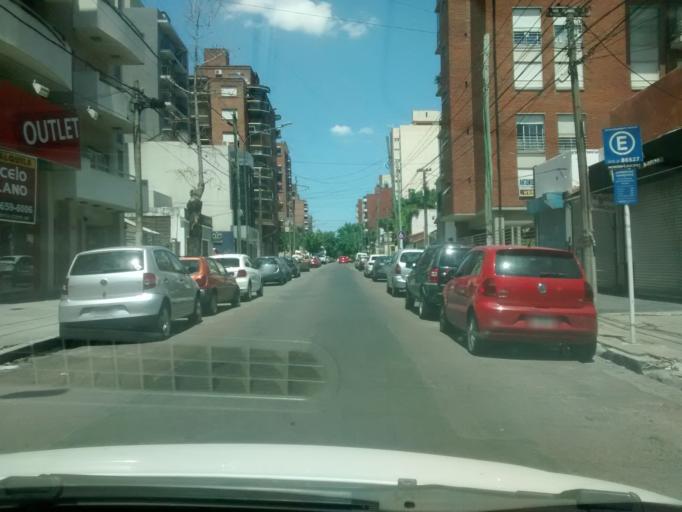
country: AR
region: Buenos Aires
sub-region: Partido de Moron
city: Moron
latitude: -34.6507
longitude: -58.6162
